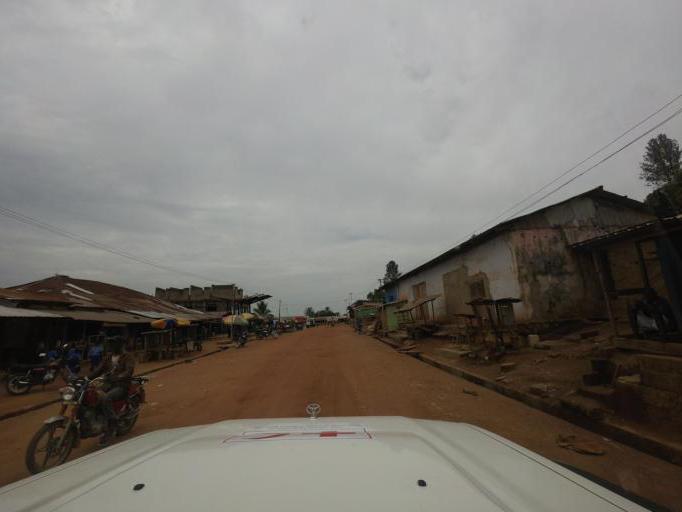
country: SL
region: Eastern Province
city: Buedu
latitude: 8.3593
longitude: -10.2079
